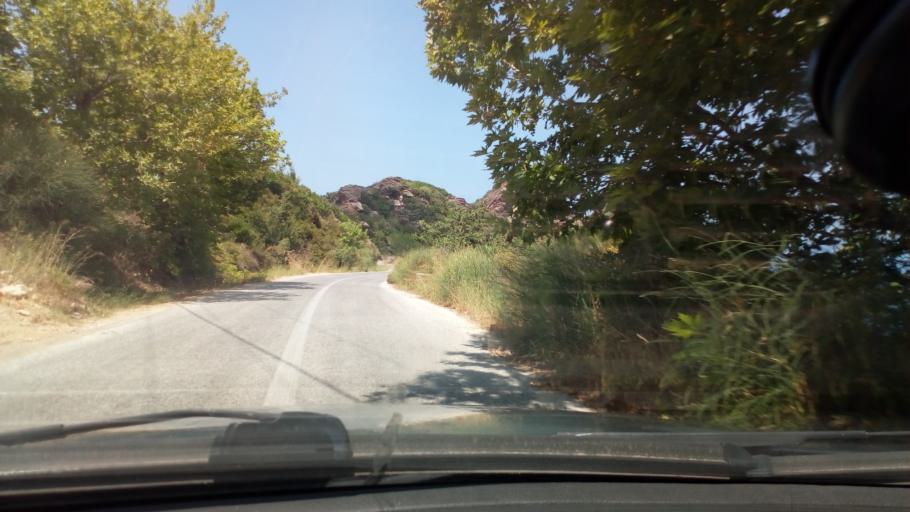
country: GR
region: North Aegean
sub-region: Nomos Samou
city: Agios Kirykos
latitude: 37.6427
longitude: 26.2622
